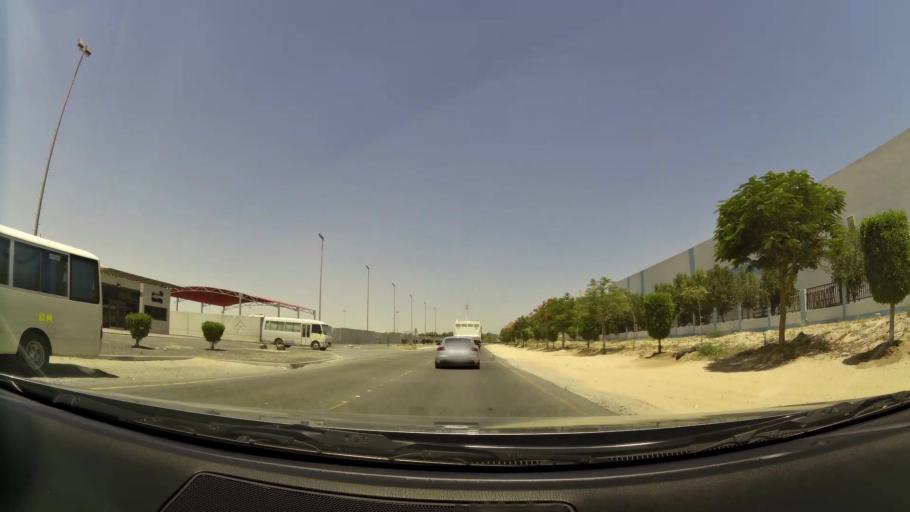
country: AE
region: Dubai
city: Dubai
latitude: 24.9658
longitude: 55.2011
